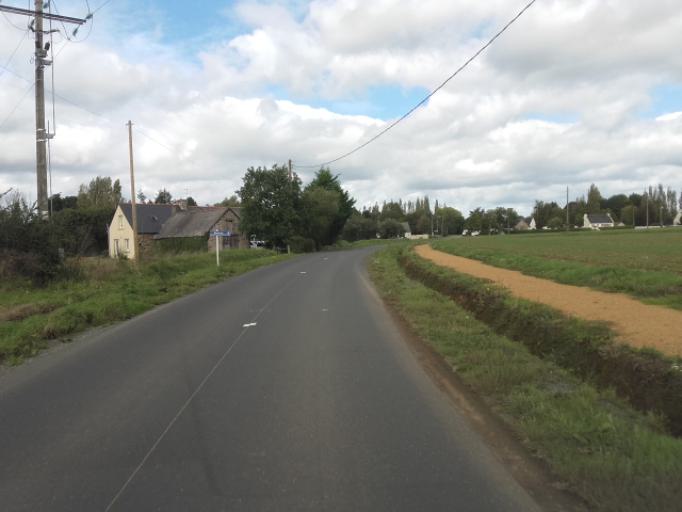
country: FR
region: Brittany
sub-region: Departement des Cotes-d'Armor
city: Lanvollon
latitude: 48.6225
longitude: -2.9863
